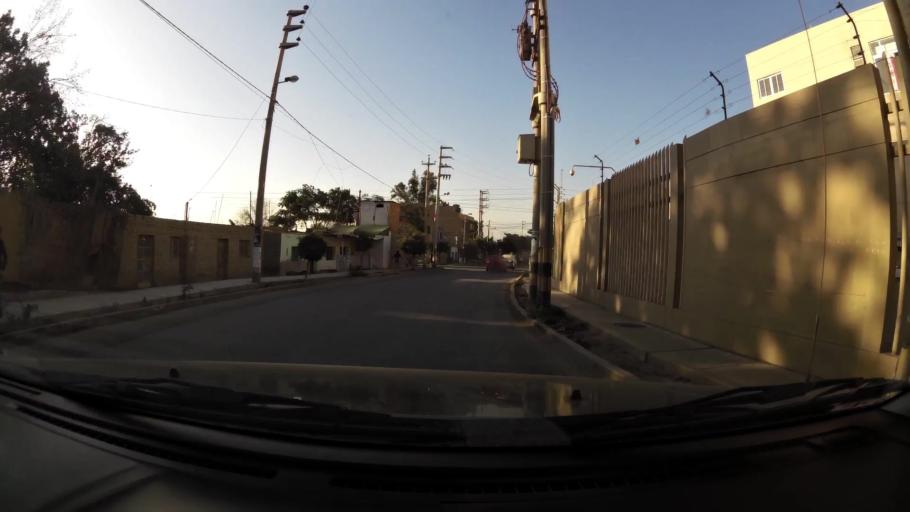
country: PE
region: Ica
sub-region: Provincia de Ica
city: Ica
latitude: -14.0566
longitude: -75.7305
